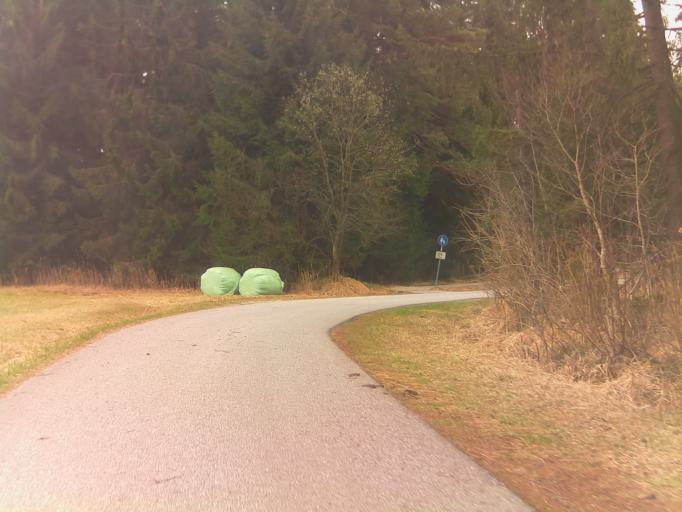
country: DE
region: Bavaria
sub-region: Upper Bavaria
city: Uffing
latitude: 47.7009
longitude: 11.1290
